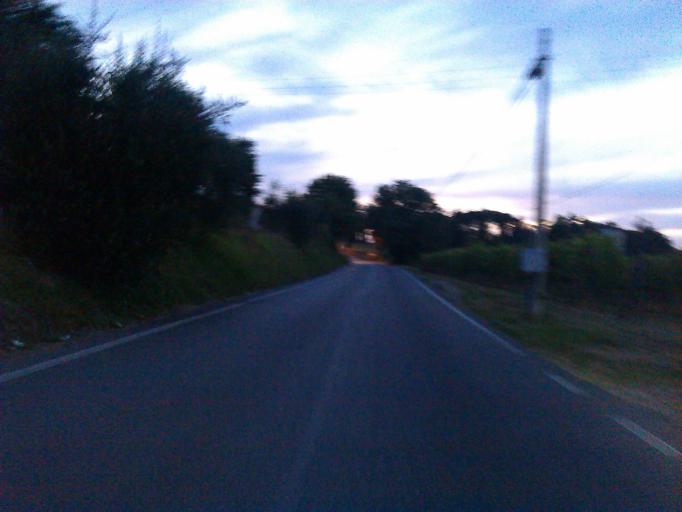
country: IT
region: Tuscany
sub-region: Province of Arezzo
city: Battifolle-Ruscello-Poggiola
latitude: 43.4484
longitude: 11.7963
